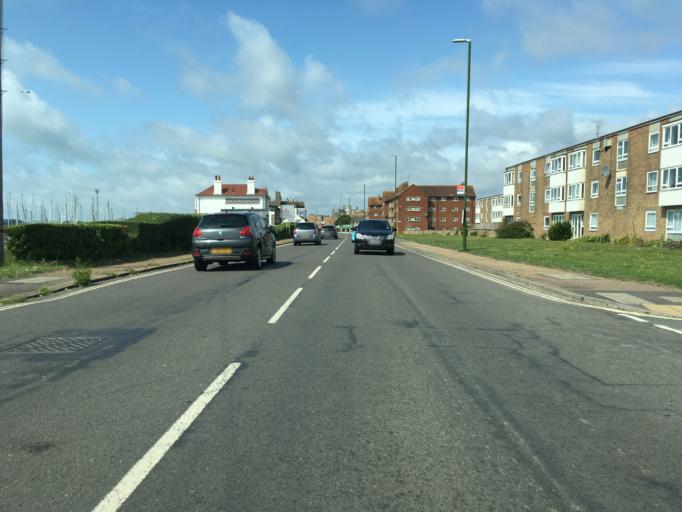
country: GB
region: England
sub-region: East Sussex
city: Portslade
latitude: 50.8315
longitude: -0.2325
